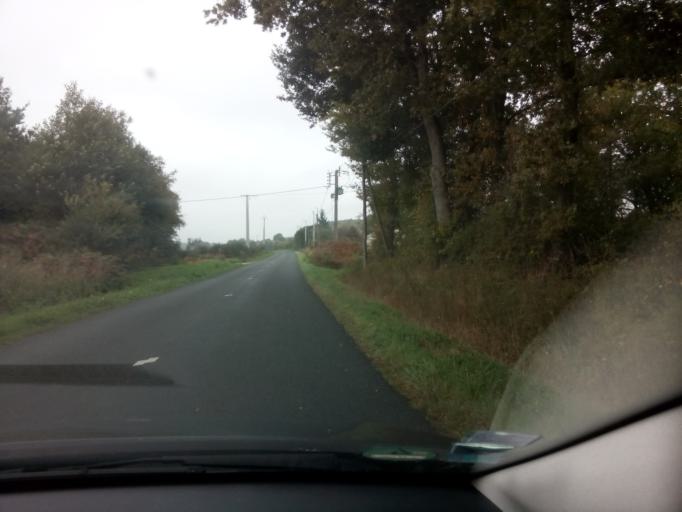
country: FR
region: Pays de la Loire
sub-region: Departement de Maine-et-Loire
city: Soulaire-et-Bourg
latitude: 47.6176
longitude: -0.5462
